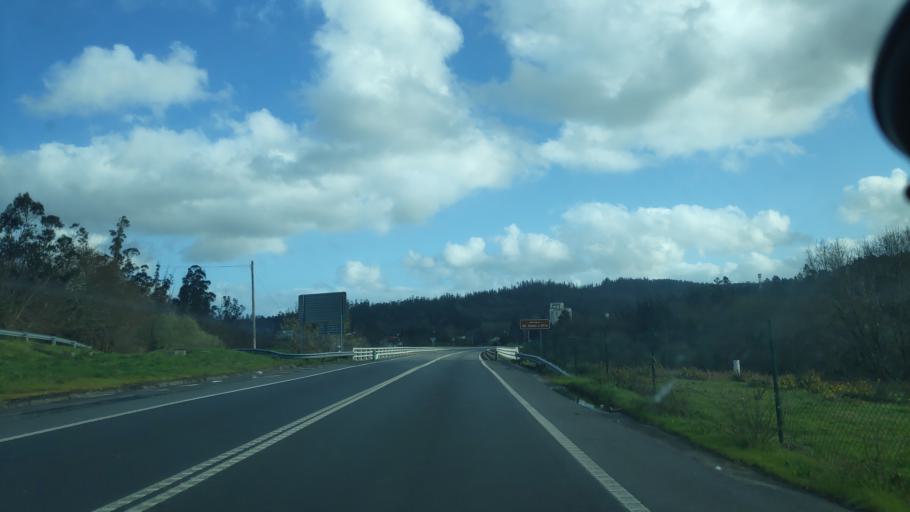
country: ES
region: Galicia
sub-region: Provincia da Coruna
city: Negreira
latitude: 42.9023
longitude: -8.7071
